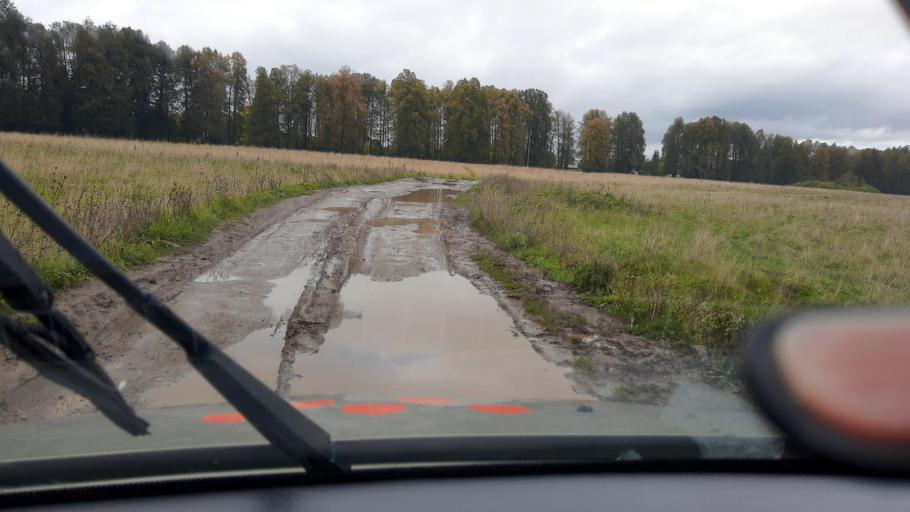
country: RU
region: Bashkortostan
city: Kudeyevskiy
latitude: 54.8769
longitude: 56.6288
